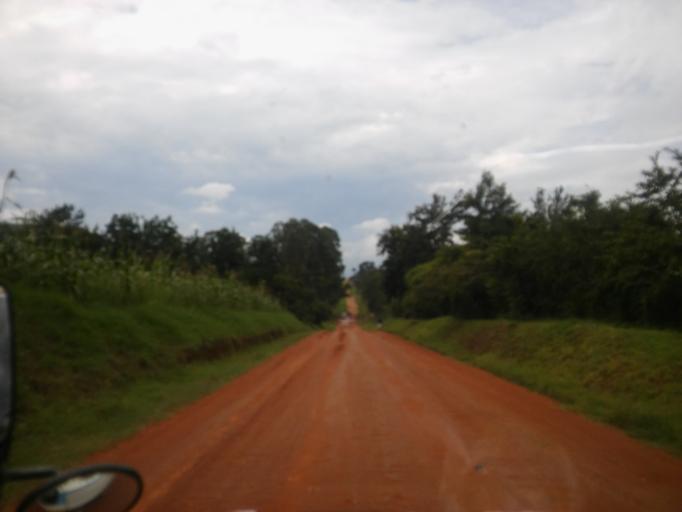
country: UG
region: Eastern Region
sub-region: Bududa District
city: Bududa
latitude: 0.9488
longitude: 34.2476
